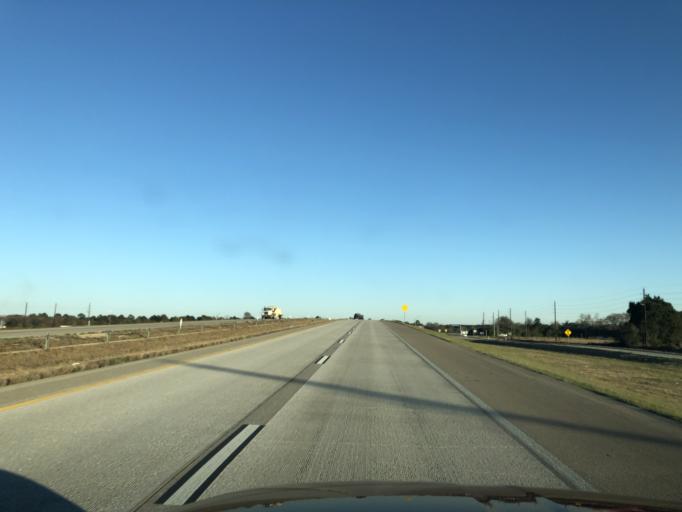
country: US
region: Texas
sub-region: Harris County
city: Cypress
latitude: 30.0530
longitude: -95.7009
